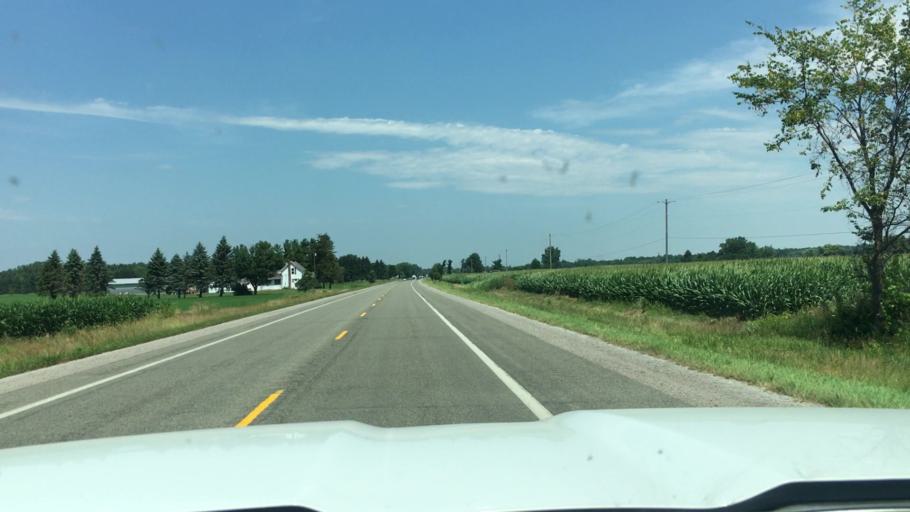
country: US
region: Michigan
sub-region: Saginaw County
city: Chesaning
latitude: 43.1947
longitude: -84.1693
